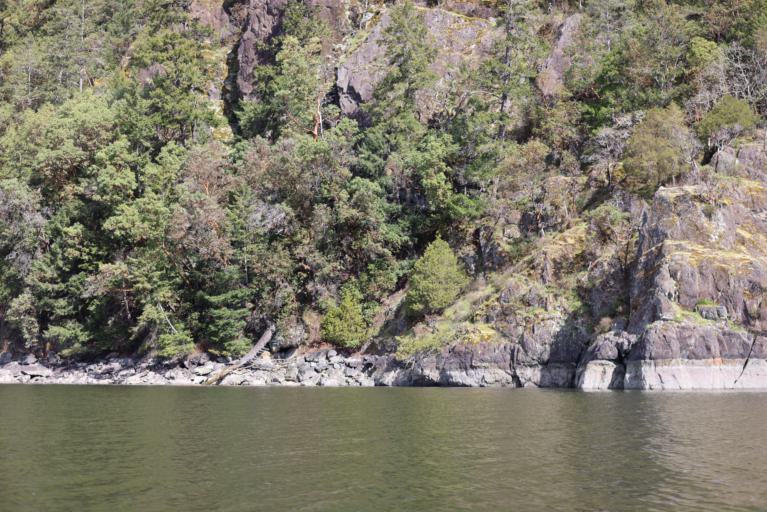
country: CA
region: British Columbia
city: Langford
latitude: 48.5610
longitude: -123.5275
